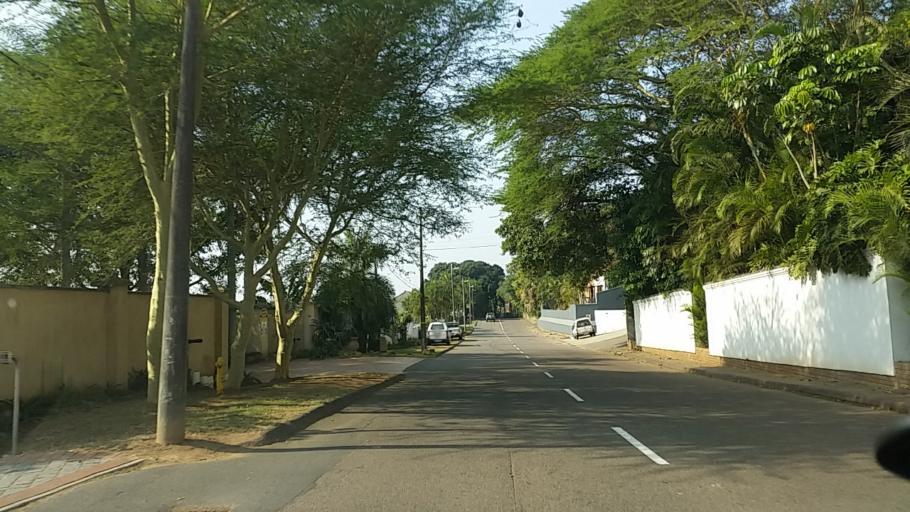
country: ZA
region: KwaZulu-Natal
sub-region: eThekwini Metropolitan Municipality
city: Berea
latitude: -29.8342
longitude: 30.9260
